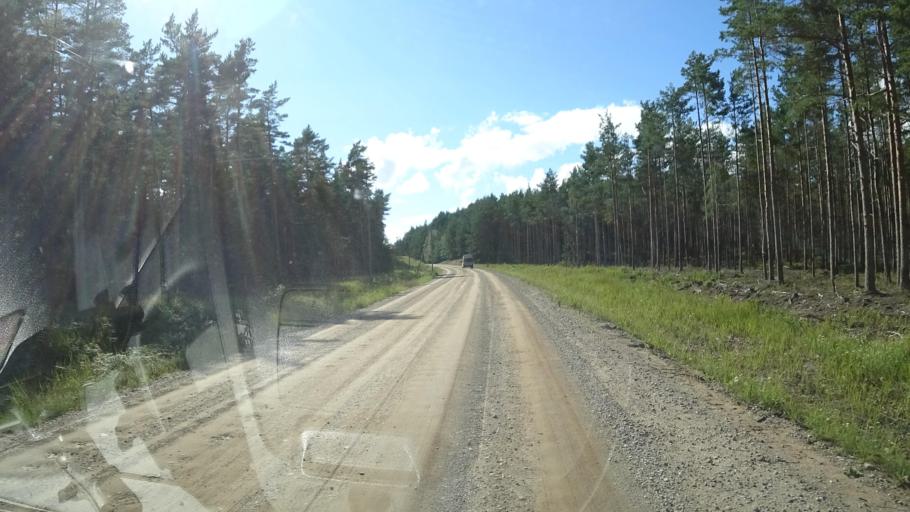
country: LV
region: Ventspils
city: Ventspils
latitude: 57.4885
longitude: 21.6691
